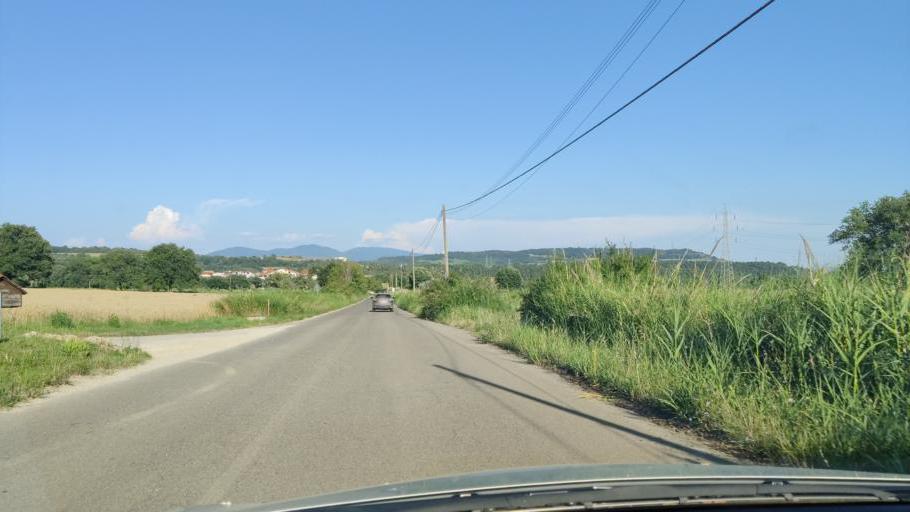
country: IT
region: Latium
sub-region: Provincia di Viterbo
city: Orte
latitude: 42.4697
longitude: 12.3835
